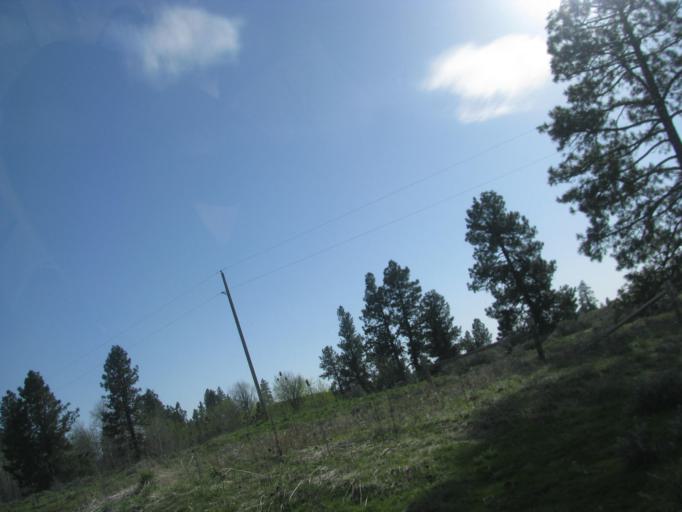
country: US
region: Washington
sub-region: Spokane County
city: Medical Lake
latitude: 47.3665
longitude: -117.8298
